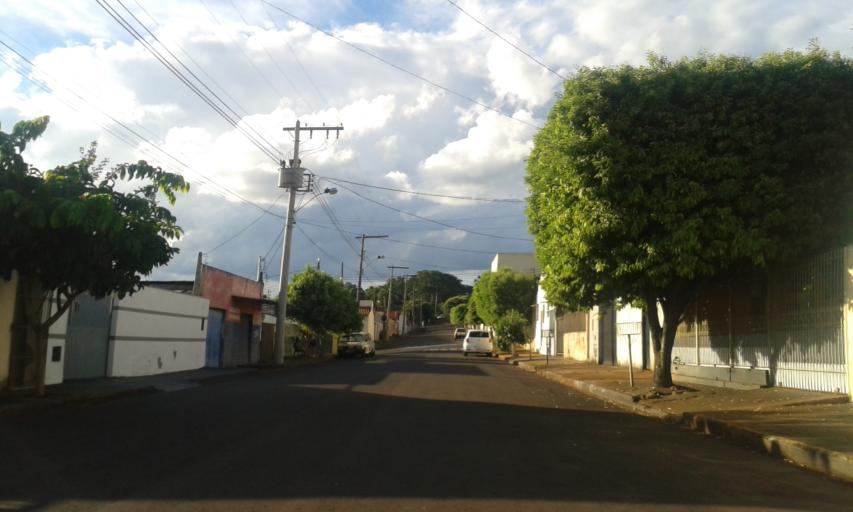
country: BR
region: Minas Gerais
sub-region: Ituiutaba
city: Ituiutaba
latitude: -18.9639
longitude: -49.4597
